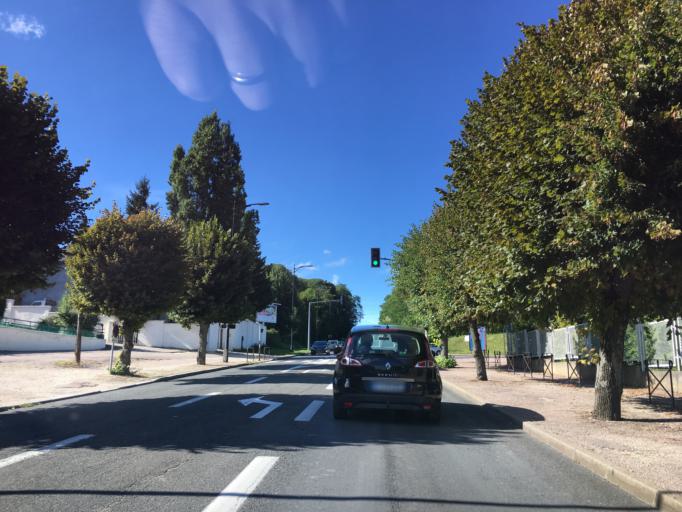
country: FR
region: Bourgogne
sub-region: Departement de l'Yonne
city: Auxerre
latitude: 47.8089
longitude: 3.5641
